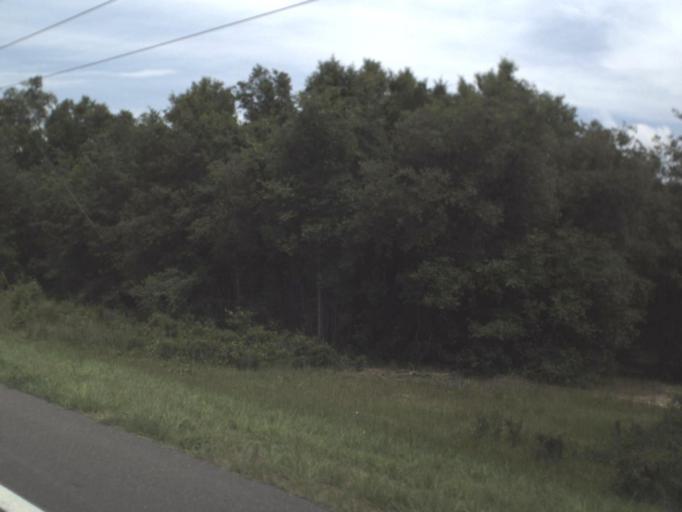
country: US
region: Florida
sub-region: Putnam County
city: Interlachen
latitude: 29.6253
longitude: -81.9449
